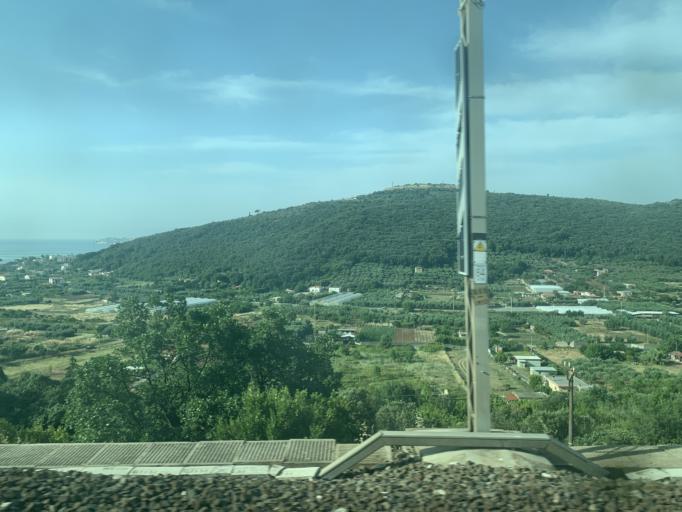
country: IT
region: Latium
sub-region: Provincia di Latina
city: Gaeta
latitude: 41.2557
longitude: 13.5719
